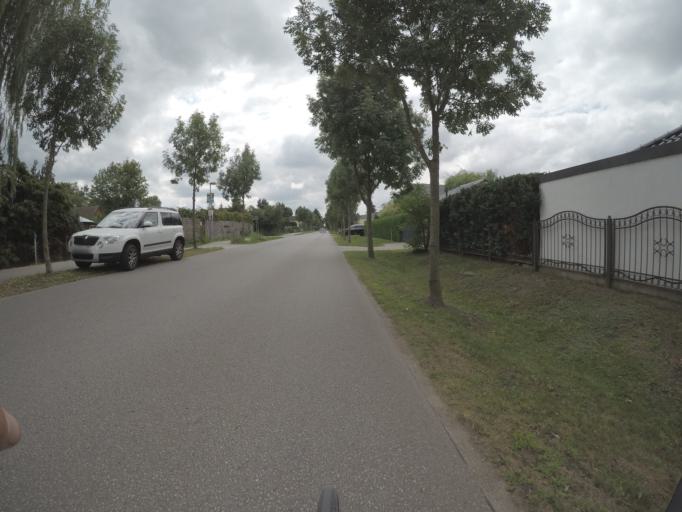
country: DE
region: Brandenburg
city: Brieselang
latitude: 52.5967
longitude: 12.9876
